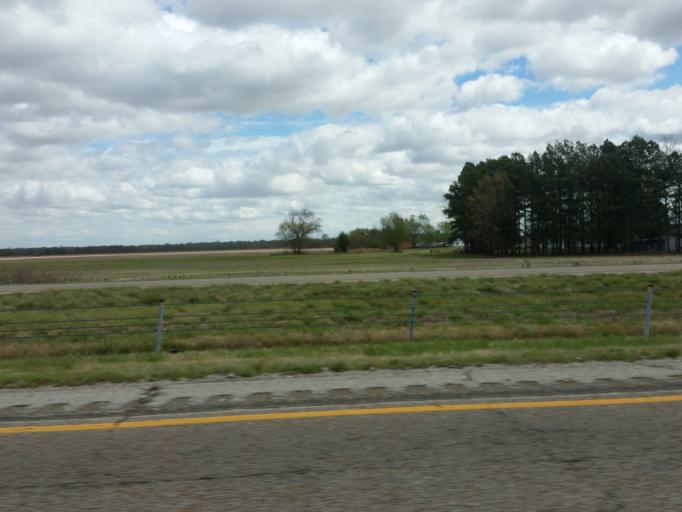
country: US
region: Arkansas
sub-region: Poinsett County
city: Trumann
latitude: 35.6099
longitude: -90.4968
